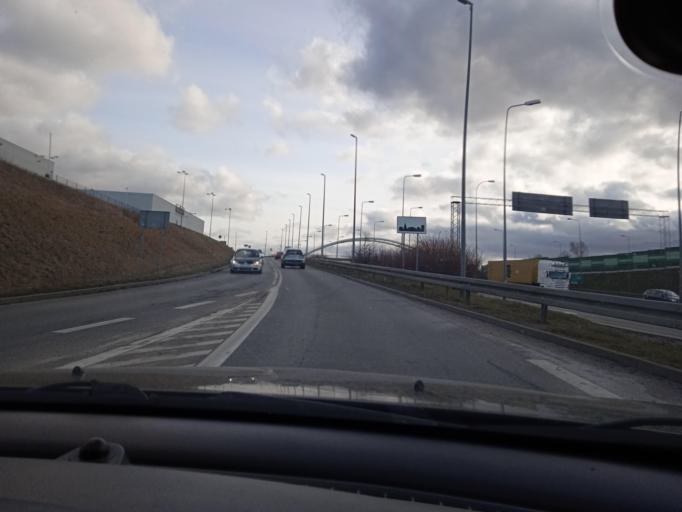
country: PL
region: Pomeranian Voivodeship
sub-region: Powiat gdanski
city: Kowale
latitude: 54.3546
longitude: 18.5199
